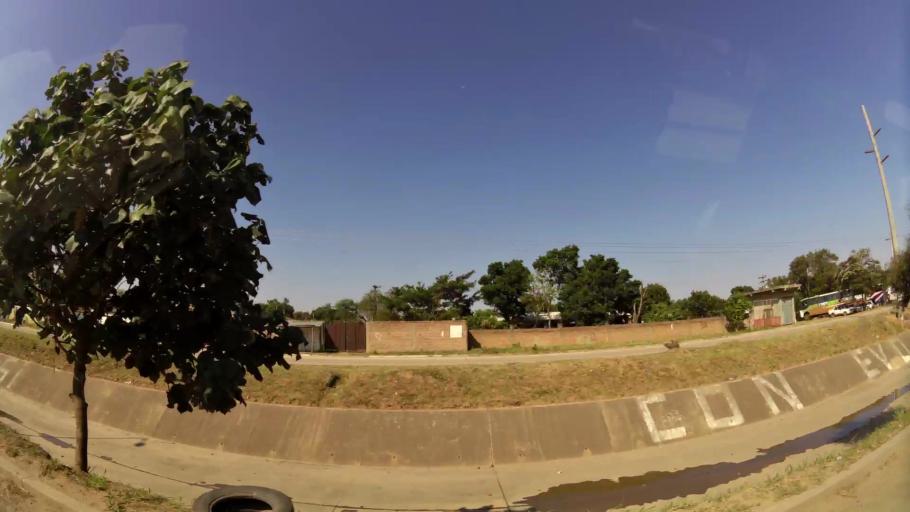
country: BO
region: Santa Cruz
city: Cotoca
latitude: -17.8095
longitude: -63.1096
